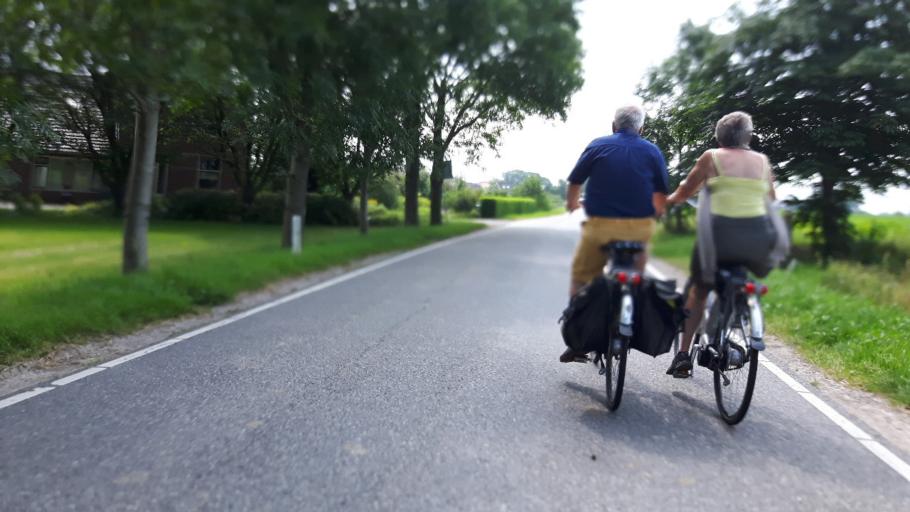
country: NL
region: Utrecht
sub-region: Gemeente IJsselstein
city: IJsselstein
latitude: 52.0517
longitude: 5.0183
